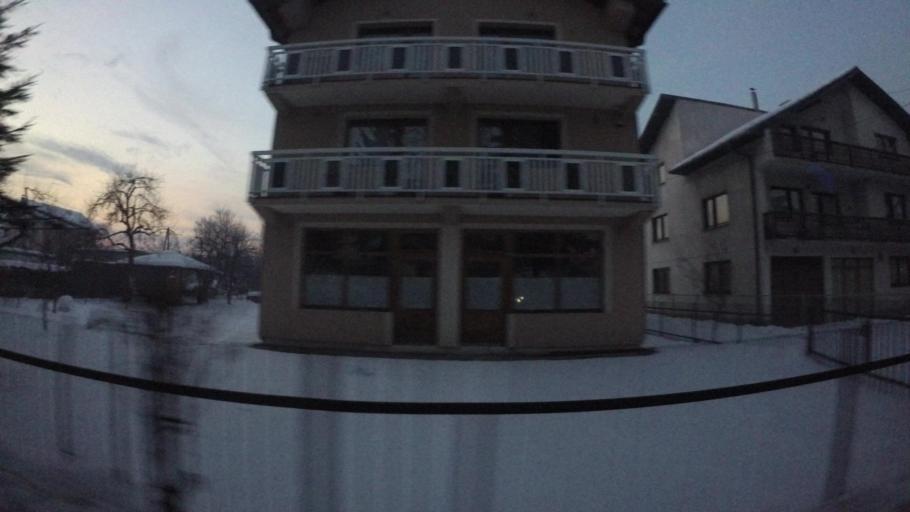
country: BA
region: Federation of Bosnia and Herzegovina
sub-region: Kanton Sarajevo
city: Sarajevo
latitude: 43.8345
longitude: 18.3212
